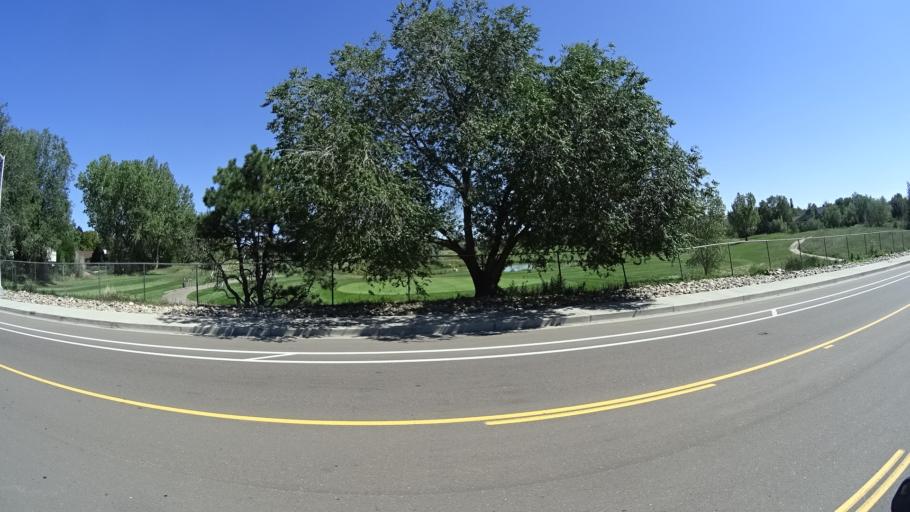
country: US
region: Colorado
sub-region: El Paso County
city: Stratmoor
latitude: 38.8215
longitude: -104.7680
